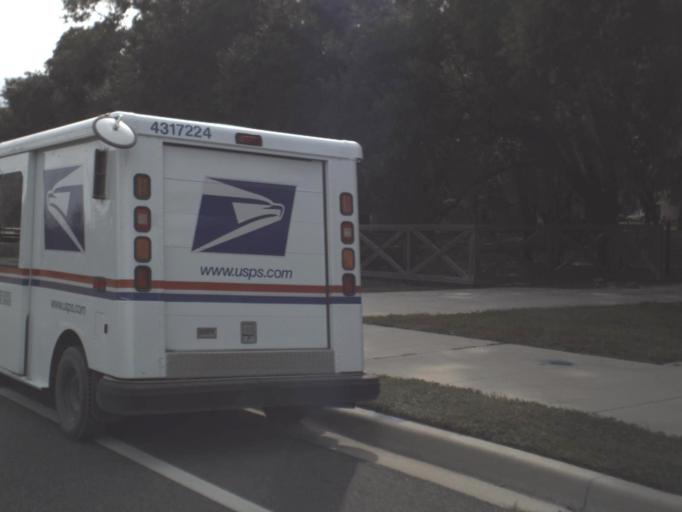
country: US
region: Florida
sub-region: Osceola County
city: Saint Cloud
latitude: 28.2824
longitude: -81.2441
